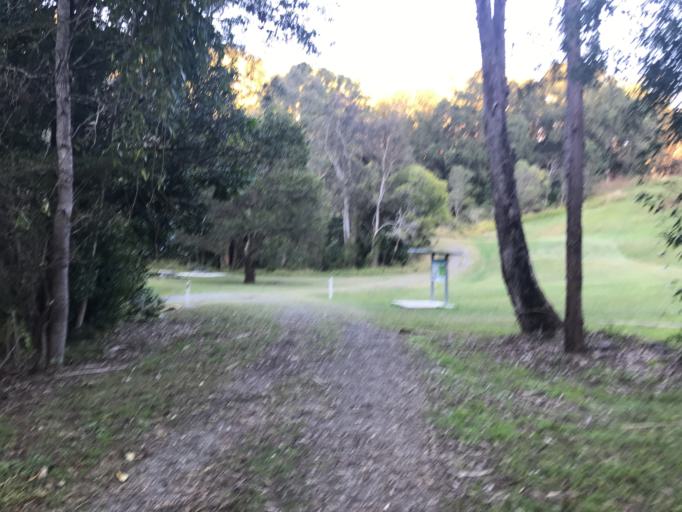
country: AU
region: Queensland
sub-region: Brisbane
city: Pullenvale
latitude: -27.4618
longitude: 152.8827
